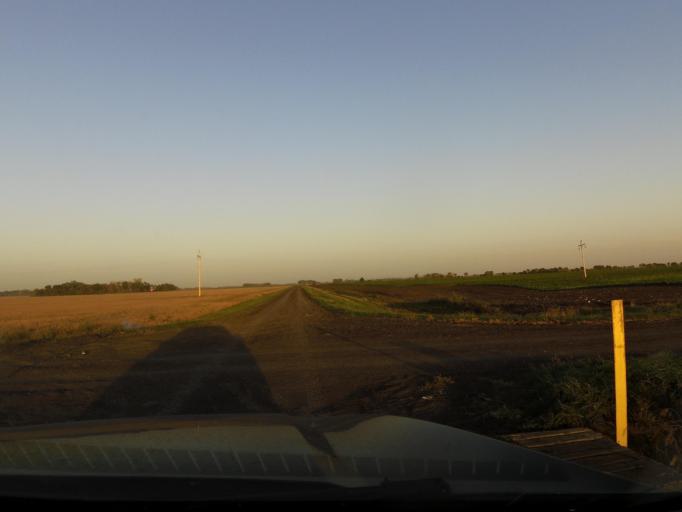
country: US
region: North Dakota
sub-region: Walsh County
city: Grafton
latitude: 48.3832
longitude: -97.2335
